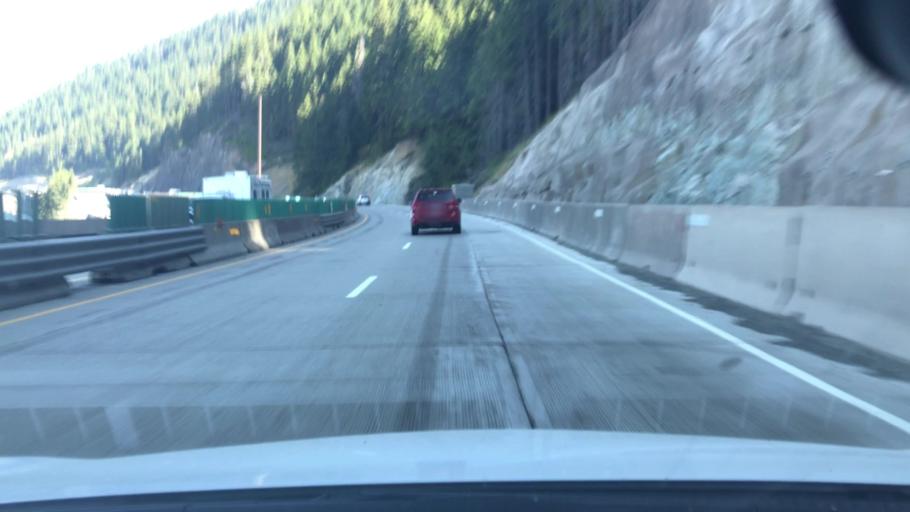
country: US
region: Washington
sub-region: King County
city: Tanner
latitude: 47.3481
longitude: -121.3634
